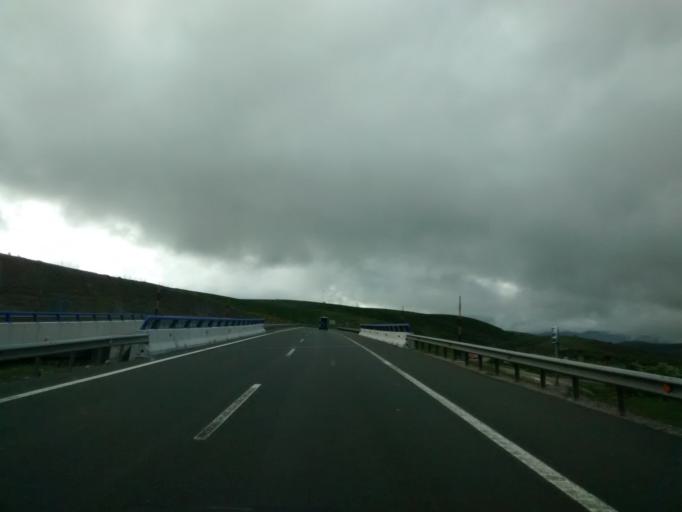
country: ES
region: Cantabria
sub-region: Provincia de Cantabria
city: Mataporquera
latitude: 42.9143
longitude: -4.1190
